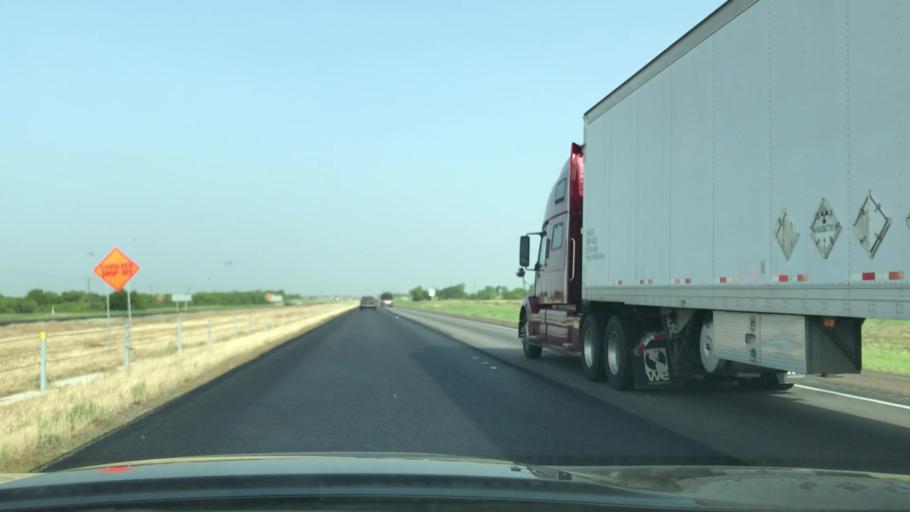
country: US
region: Texas
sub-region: Kaufman County
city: Terrell
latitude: 32.6845
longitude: -96.2079
